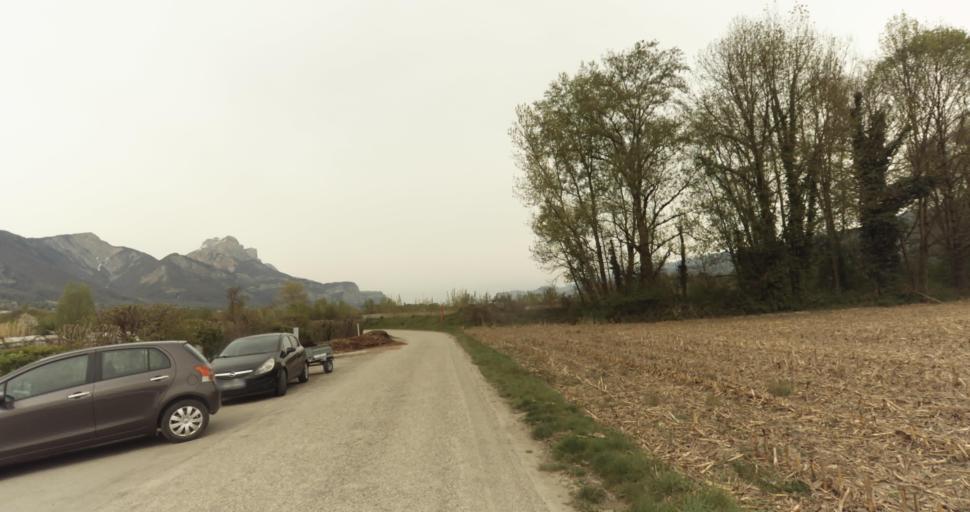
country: FR
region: Rhone-Alpes
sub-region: Departement de l'Isere
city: Domene
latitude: 45.2198
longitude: 5.8266
